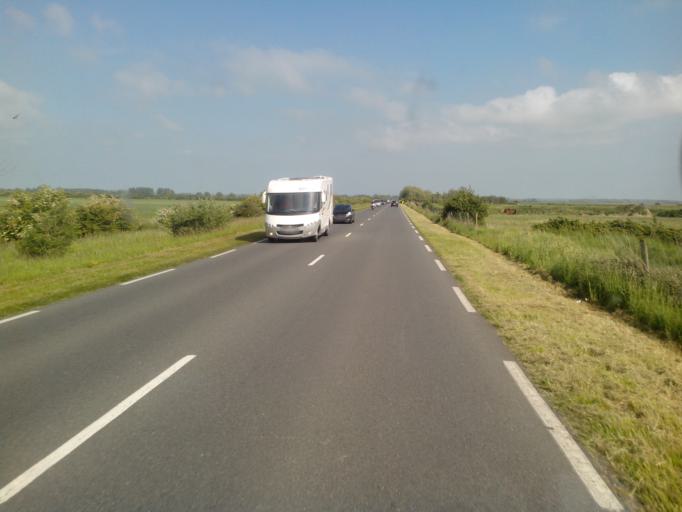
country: FR
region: Picardie
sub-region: Departement de la Somme
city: Le Crotoy
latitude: 50.2188
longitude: 1.6453
